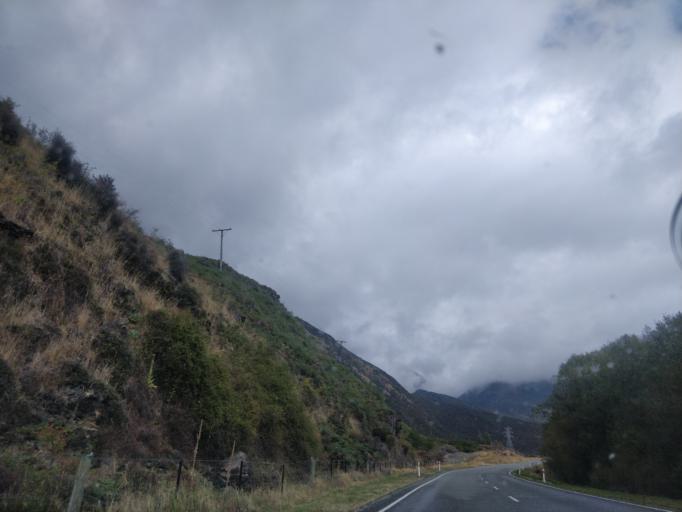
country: NZ
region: Canterbury
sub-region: Waimakariri District
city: Oxford
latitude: -43.0291
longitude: 171.6852
